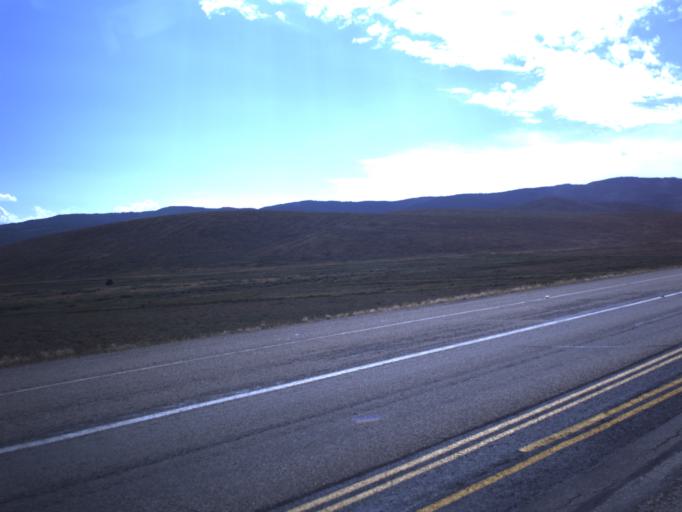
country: US
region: Utah
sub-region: Wasatch County
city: Heber
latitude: 40.2421
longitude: -111.1536
